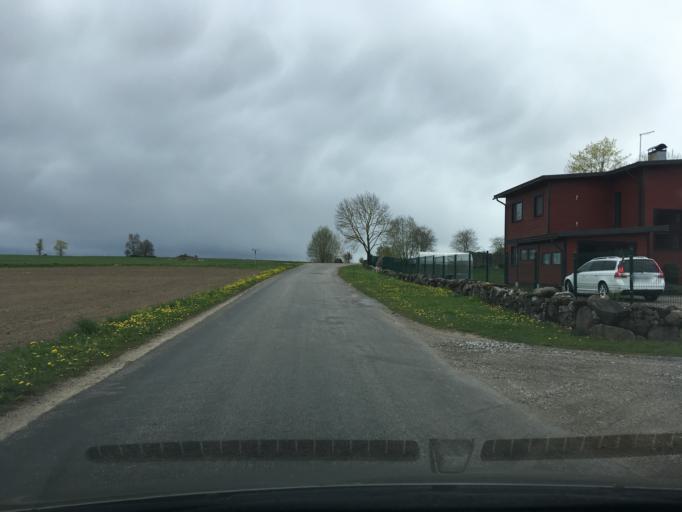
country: EE
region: Harju
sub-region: Rae vald
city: Vaida
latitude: 59.3632
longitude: 24.9701
